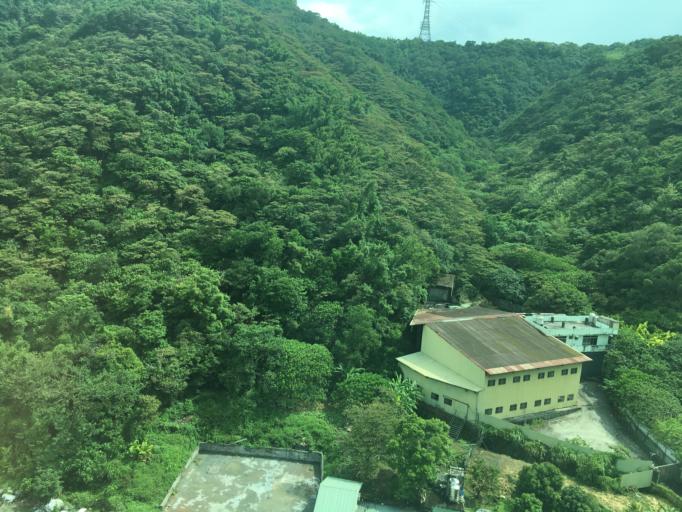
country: TW
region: Taipei
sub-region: Taipei
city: Banqiao
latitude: 25.0291
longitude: 121.4046
